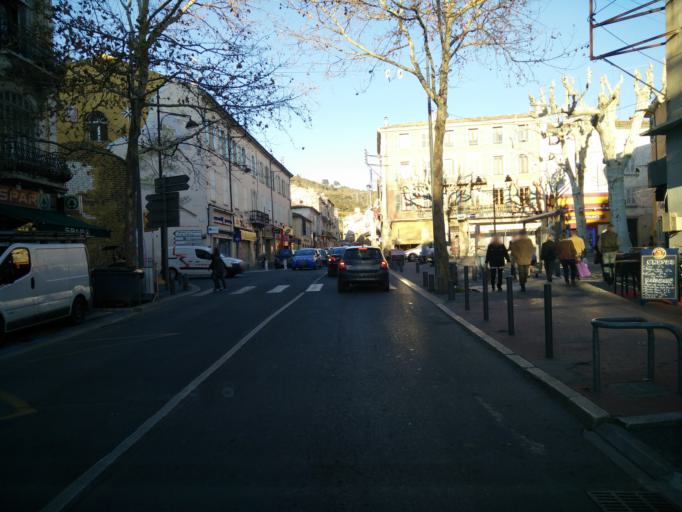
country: FR
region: Provence-Alpes-Cote d'Azur
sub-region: Departement du Var
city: Draguignan
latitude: 43.5390
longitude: 6.4629
